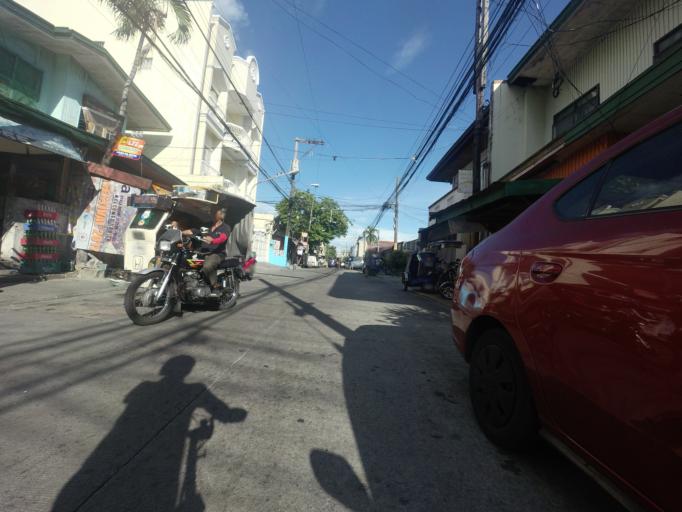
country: PH
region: Metro Manila
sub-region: San Juan
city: San Juan
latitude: 14.5887
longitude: 121.0283
